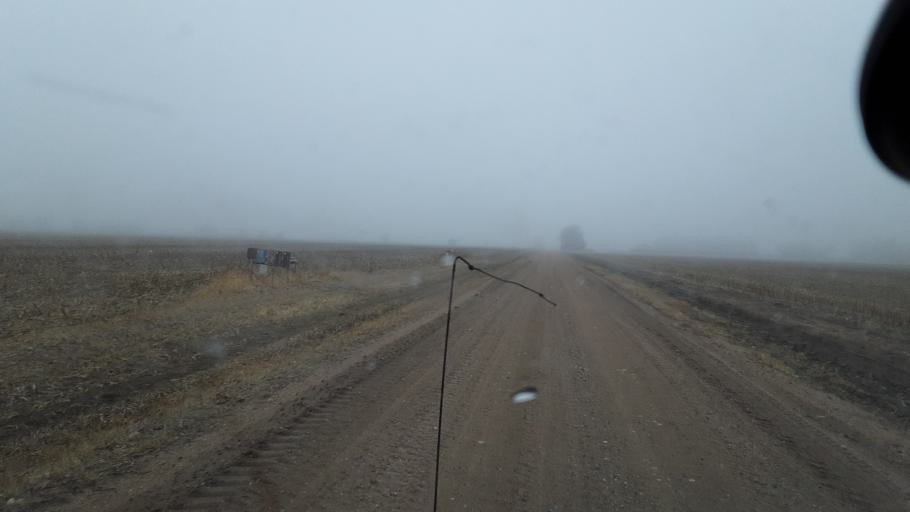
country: US
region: Kansas
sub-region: Reno County
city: South Hutchinson
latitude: 37.9553
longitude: -97.9511
